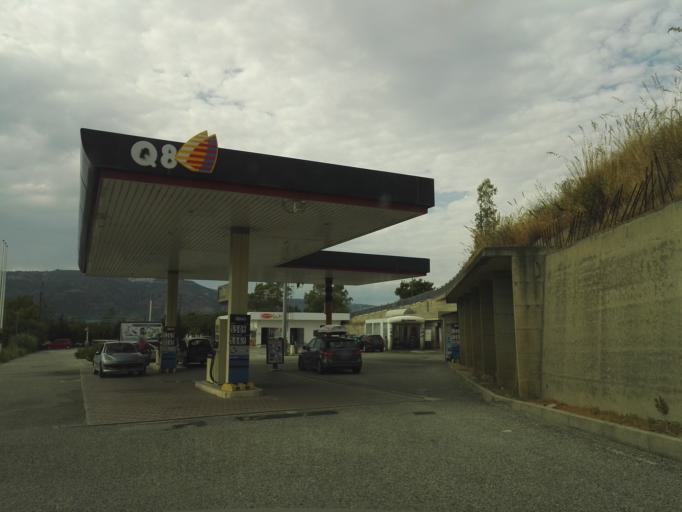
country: IT
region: Calabria
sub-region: Provincia di Catanzaro
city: Soverato Superiore
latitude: 38.6995
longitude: 16.5361
